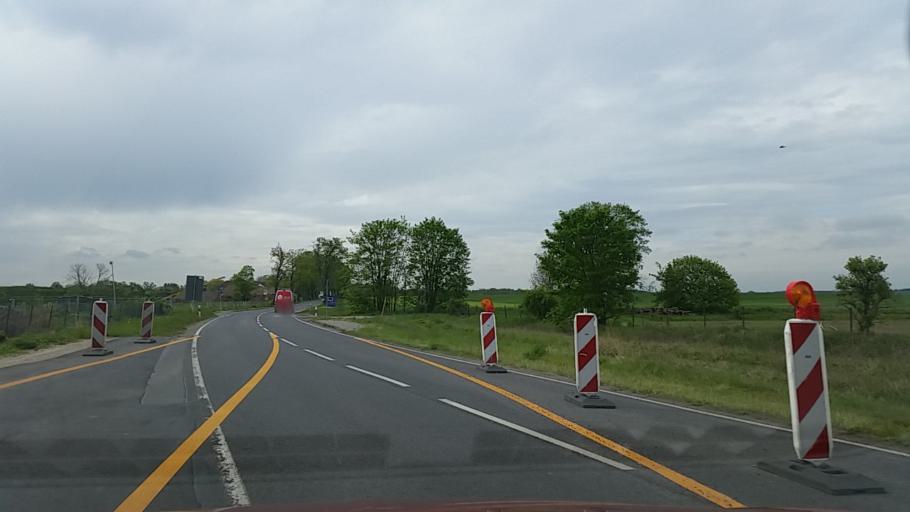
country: DE
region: Brandenburg
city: Velten
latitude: 52.7040
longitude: 13.1077
